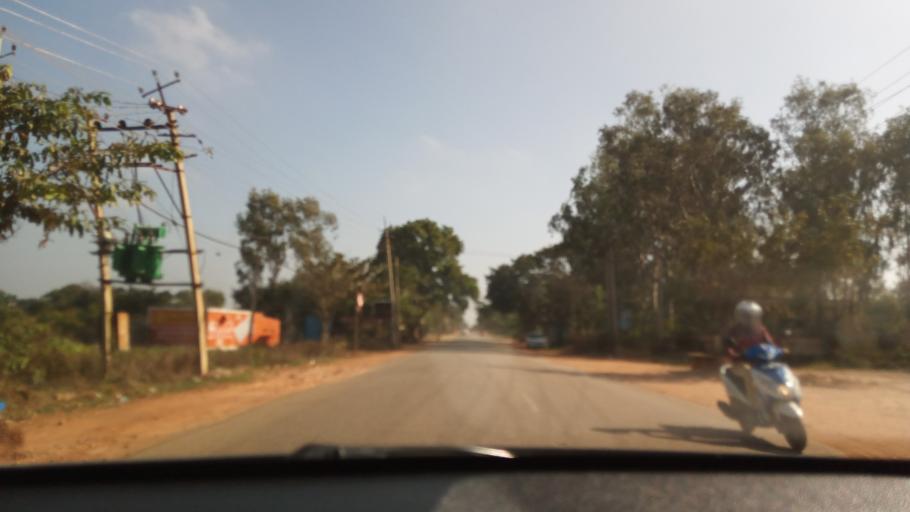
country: IN
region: Karnataka
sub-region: Bangalore Rural
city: Devanhalli
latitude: 13.2571
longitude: 77.7259
